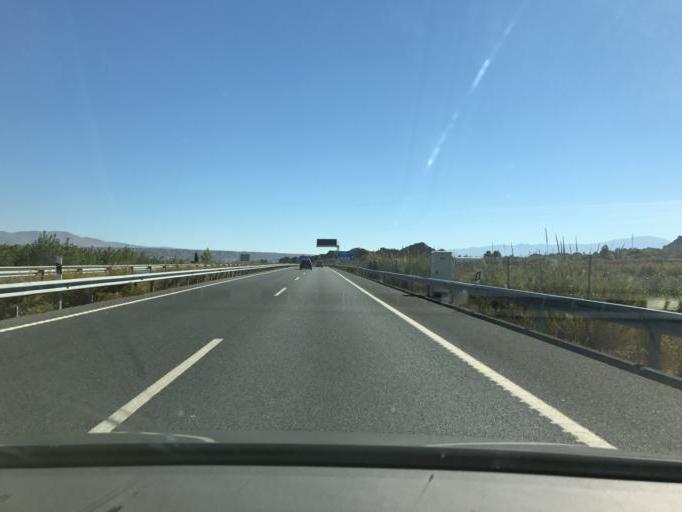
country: ES
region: Andalusia
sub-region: Provincia de Granada
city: Purullena
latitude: 37.3249
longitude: -3.1738
